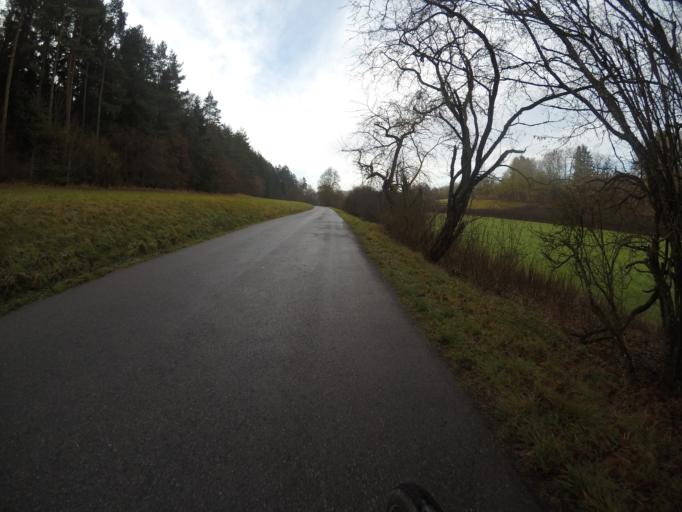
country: DE
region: Baden-Wuerttemberg
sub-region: Karlsruhe Region
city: Gechingen
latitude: 48.6737
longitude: 8.8369
